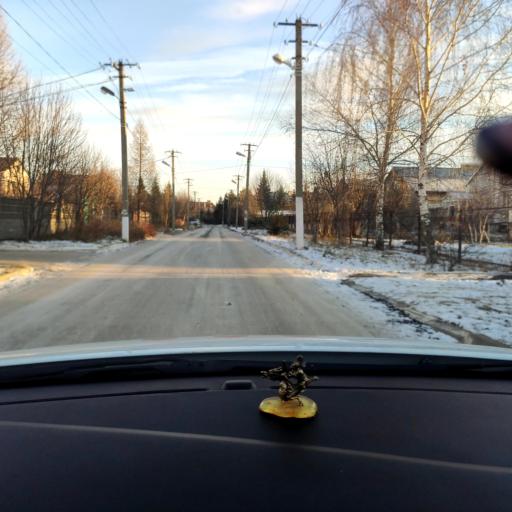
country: RU
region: Tatarstan
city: Stolbishchi
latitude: 55.6074
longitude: 49.1385
